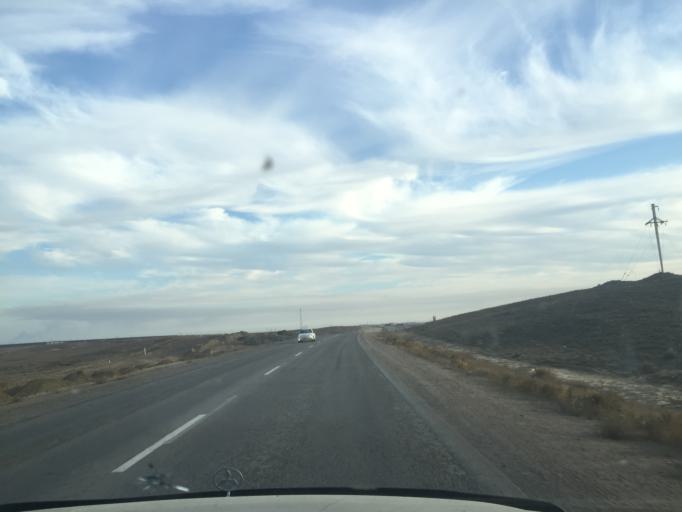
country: KZ
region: Almaty Oblysy
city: Ulken
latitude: 45.1735
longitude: 73.9323
